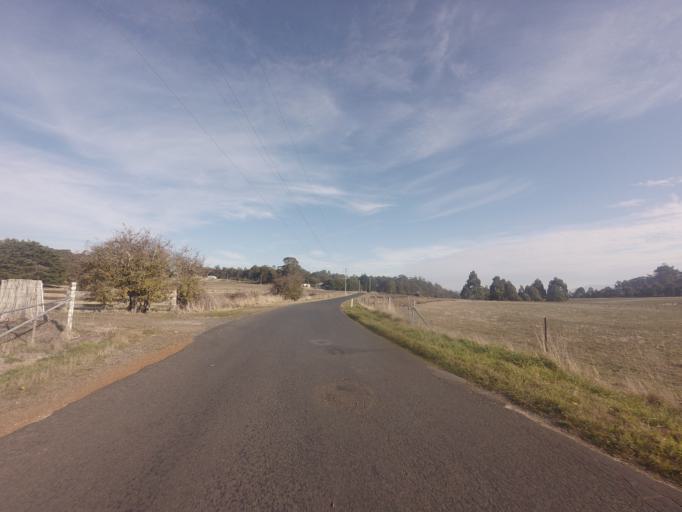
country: AU
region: Tasmania
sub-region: Sorell
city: Sorell
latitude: -42.4797
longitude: 147.4571
